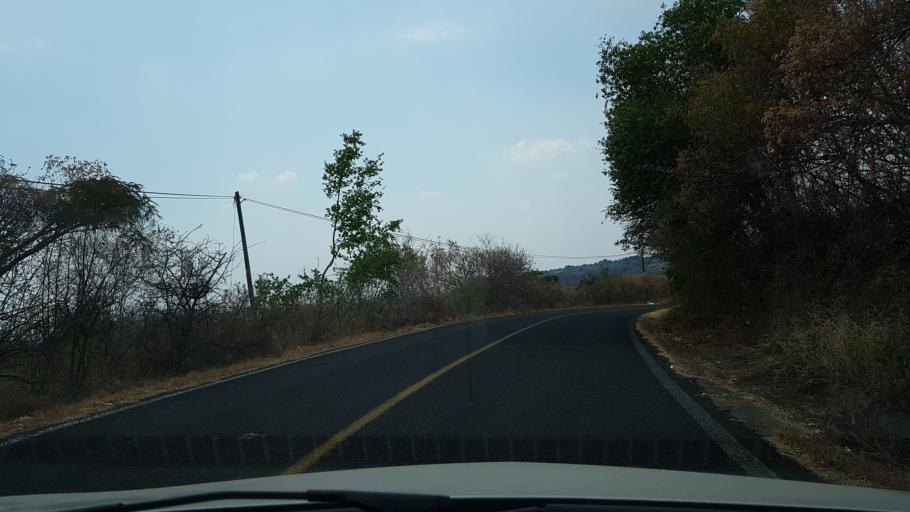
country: MX
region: Morelos
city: Tlacotepec
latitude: 18.8362
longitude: -98.7265
